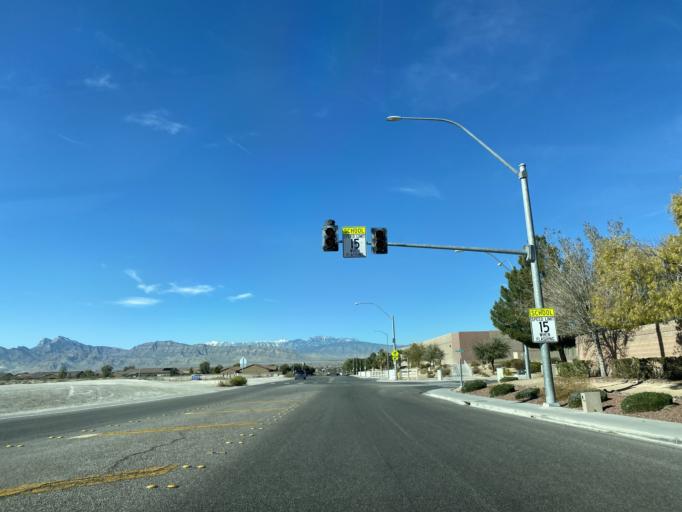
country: US
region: Nevada
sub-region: Clark County
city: North Las Vegas
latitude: 36.3051
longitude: -115.2324
